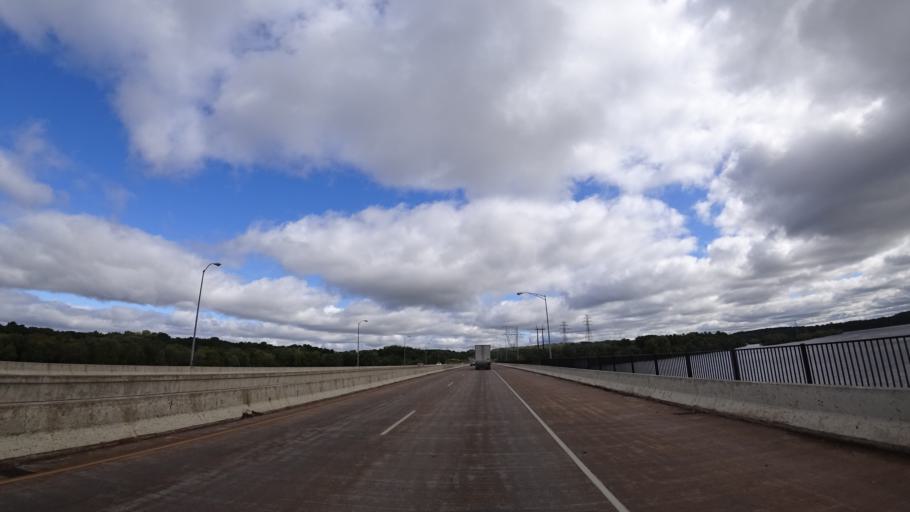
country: US
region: Wisconsin
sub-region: Eau Claire County
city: Eau Claire
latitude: 44.8409
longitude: -91.4997
